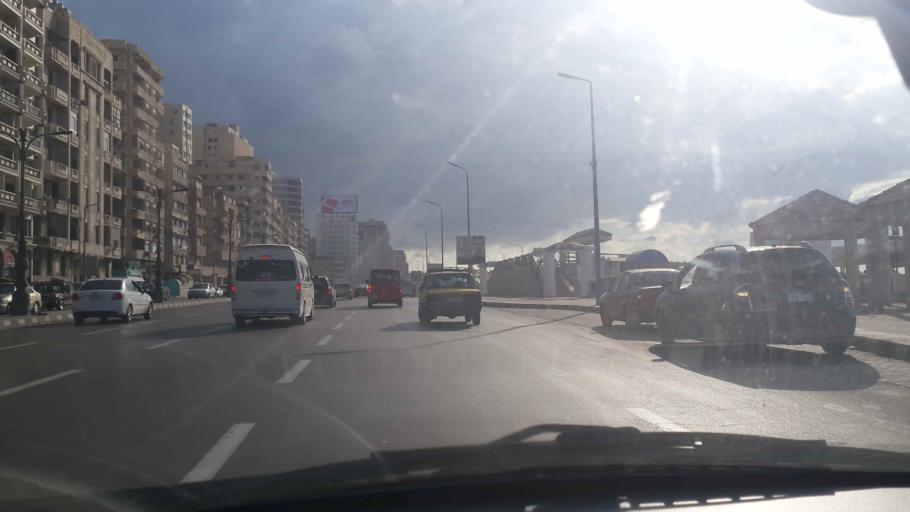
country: EG
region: Alexandria
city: Alexandria
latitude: 31.2192
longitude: 29.9276
